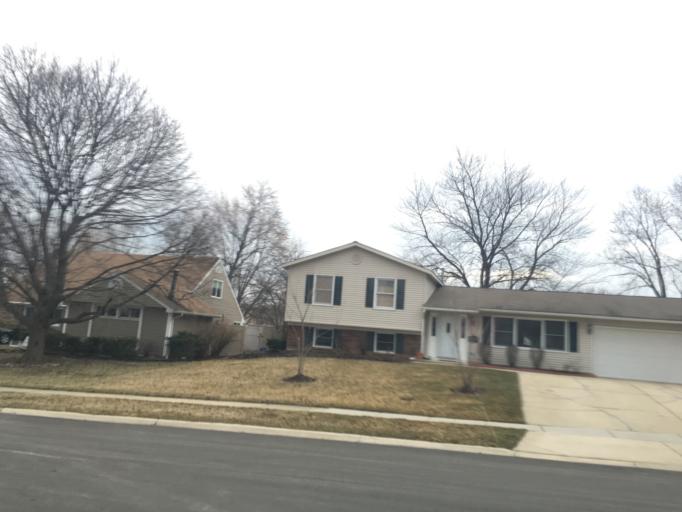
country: US
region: Illinois
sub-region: Cook County
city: Schaumburg
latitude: 42.0294
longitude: -88.1200
